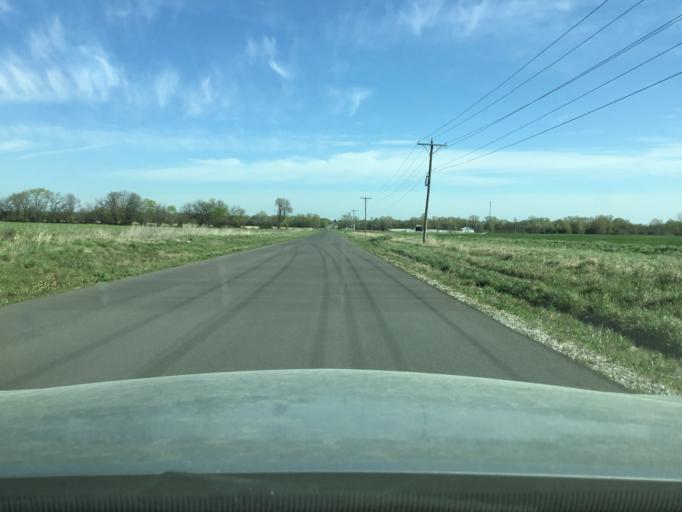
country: US
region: Kansas
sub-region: Neosho County
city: Chanute
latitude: 37.6503
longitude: -95.4435
